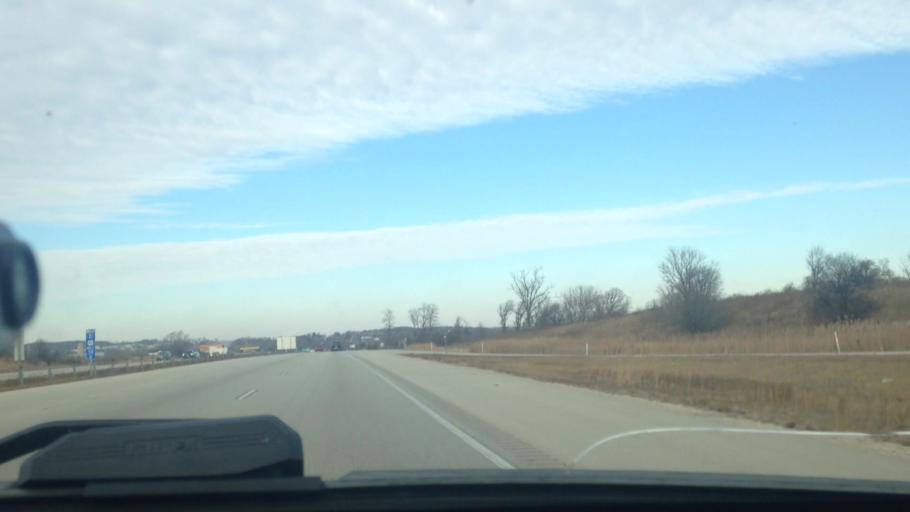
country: US
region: Wisconsin
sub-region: Washington County
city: Richfield
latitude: 43.2532
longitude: -88.1813
